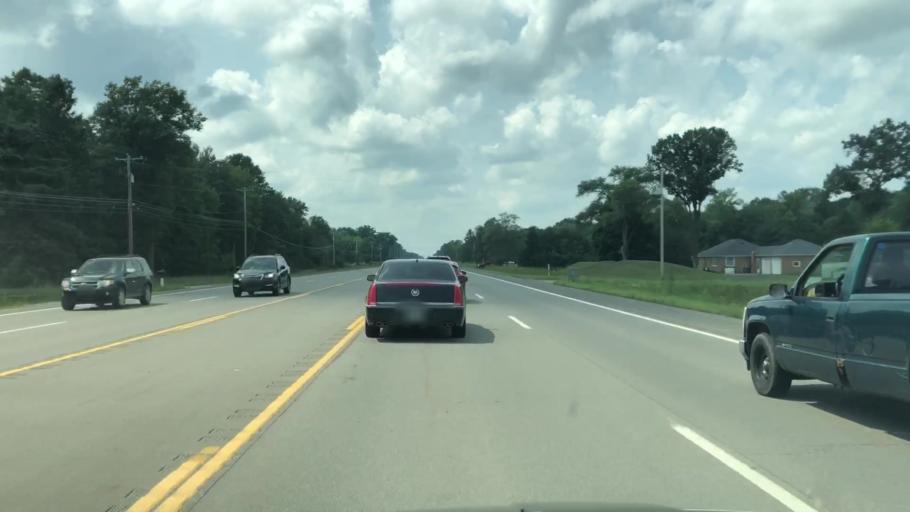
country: US
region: Michigan
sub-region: Midland County
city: Coleman
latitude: 43.6112
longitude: -84.4508
